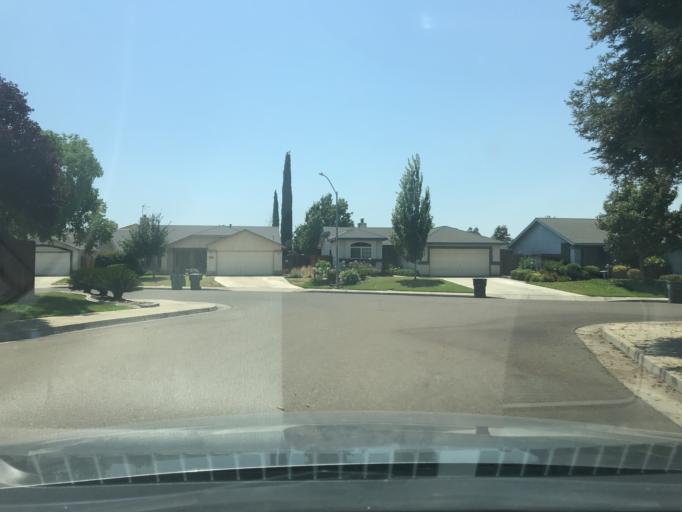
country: US
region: California
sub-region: Merced County
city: Atwater
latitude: 37.3628
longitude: -120.5990
